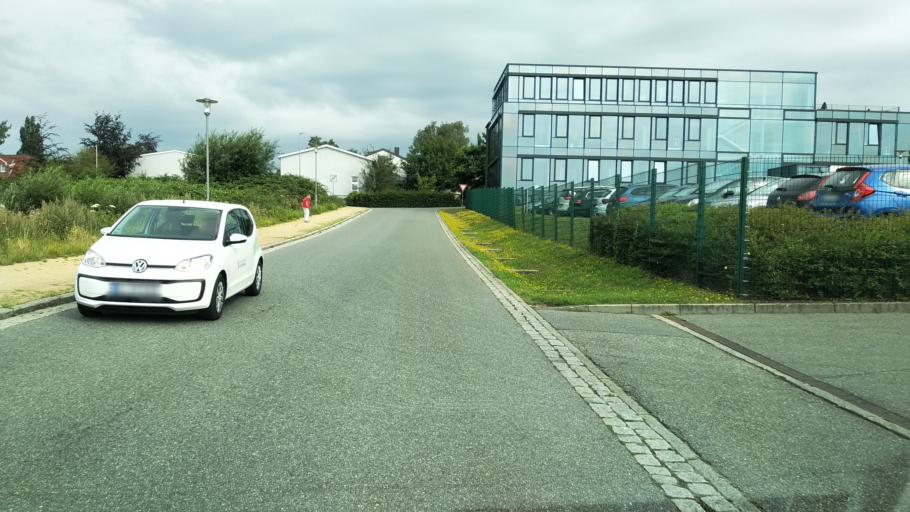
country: DE
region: Schleswig-Holstein
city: Fahrdorf
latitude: 54.5171
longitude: 9.5847
